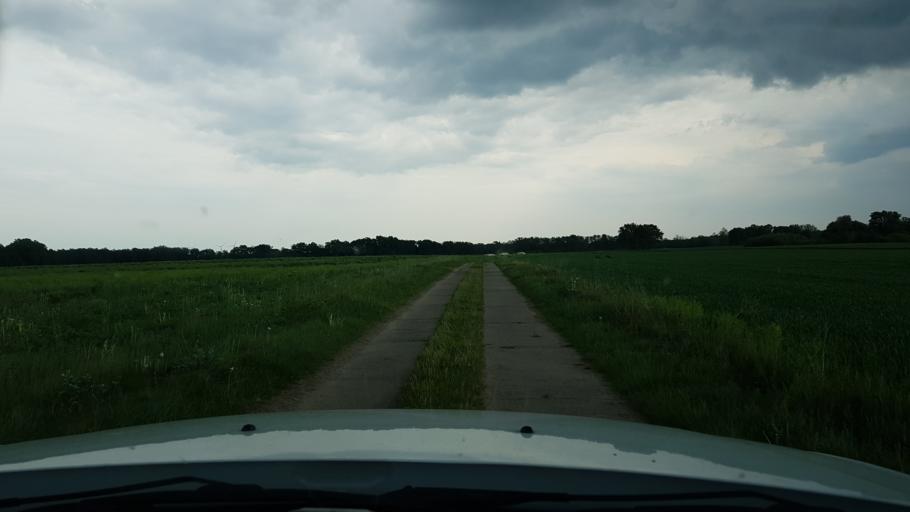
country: PL
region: West Pomeranian Voivodeship
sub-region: Powiat stargardzki
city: Stara Dabrowa
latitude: 53.3641
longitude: 15.1838
